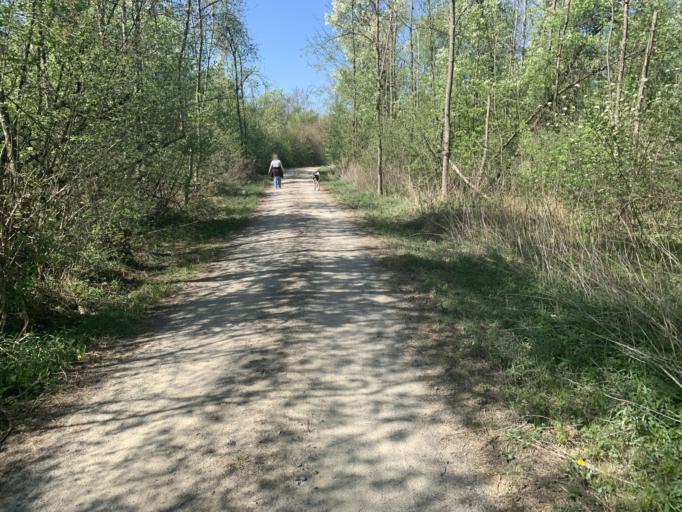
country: DE
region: Bavaria
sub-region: Swabia
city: Gersthofen
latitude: 48.4549
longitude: 10.8864
